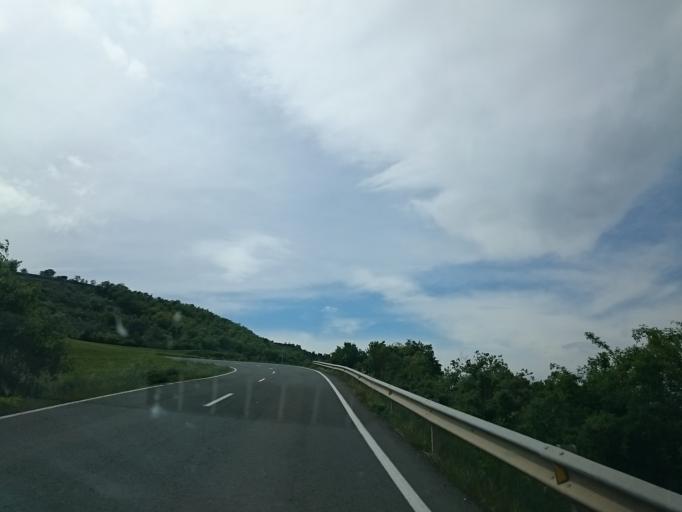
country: ES
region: Catalonia
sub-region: Provincia de Lleida
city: Ivorra
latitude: 41.7668
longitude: 1.3805
